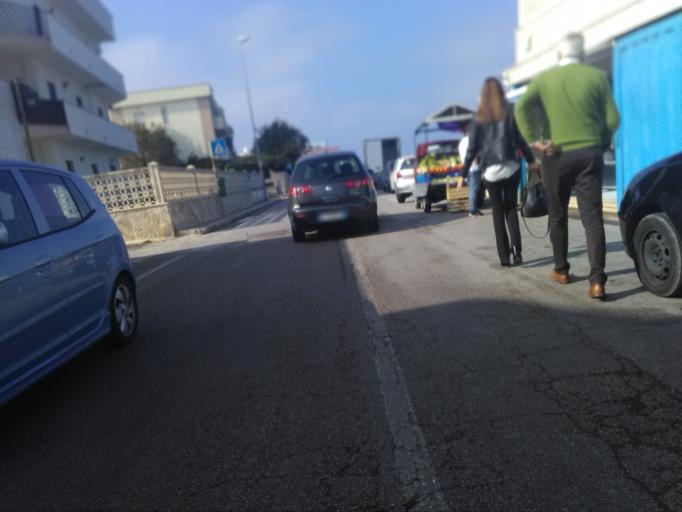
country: IT
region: Apulia
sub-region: Provincia di Bari
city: San Paolo
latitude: 41.1629
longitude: 16.7601
